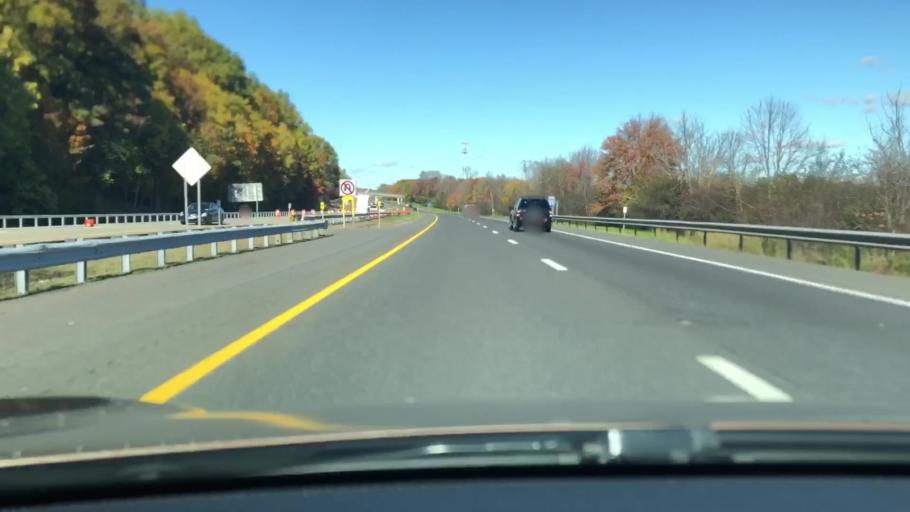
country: US
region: New York
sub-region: Orange County
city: Gardnertown
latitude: 41.5162
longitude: -74.0735
